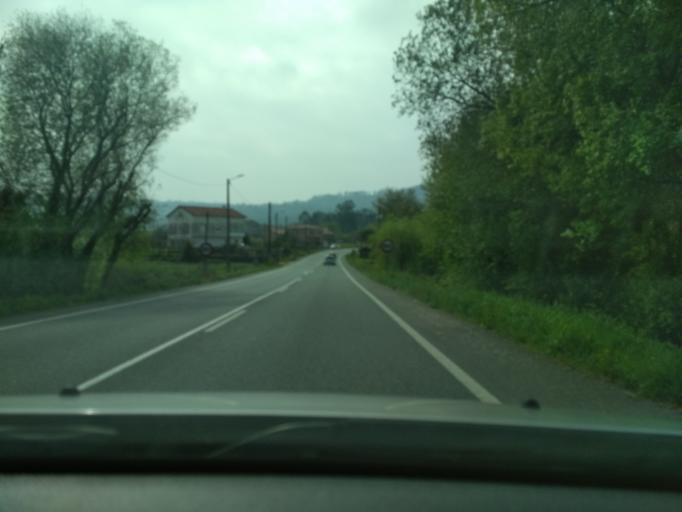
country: ES
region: Galicia
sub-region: Provincia de Pontevedra
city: Catoira
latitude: 42.6700
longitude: -8.7068
